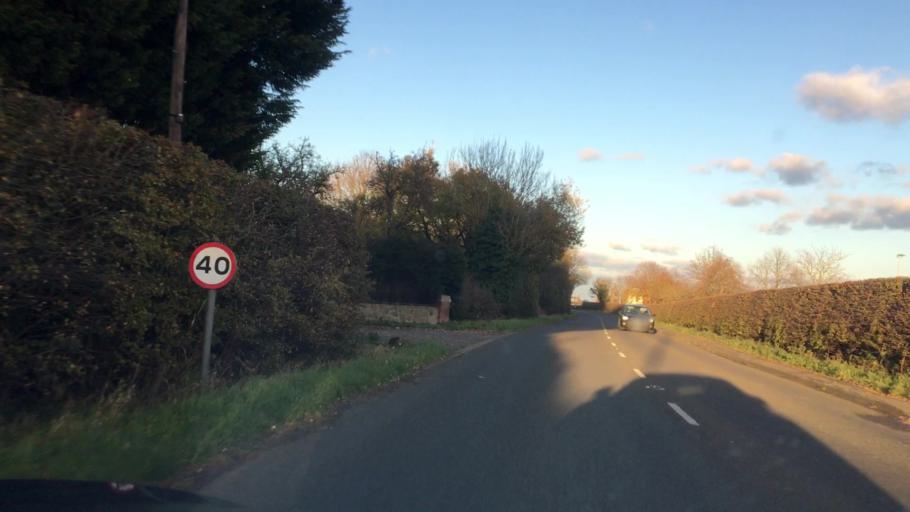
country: GB
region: England
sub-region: Derbyshire
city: Melbourne
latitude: 52.8216
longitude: -1.4420
